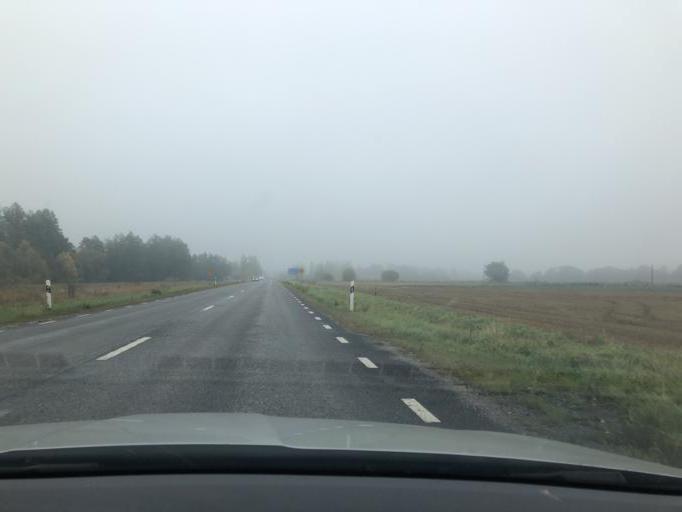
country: SE
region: Uppsala
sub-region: Tierps Kommun
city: Tierp
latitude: 60.3364
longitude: 17.5058
